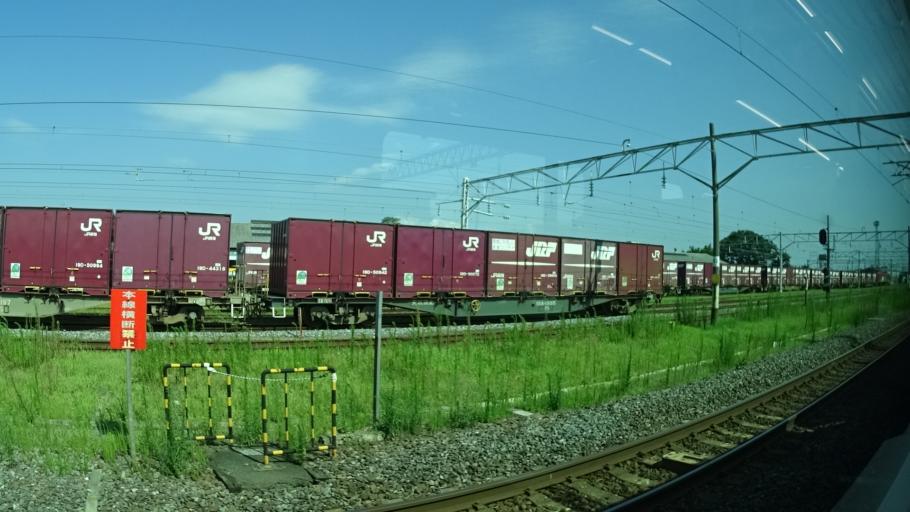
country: JP
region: Miyagi
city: Kogota
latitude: 38.5392
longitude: 141.0645
